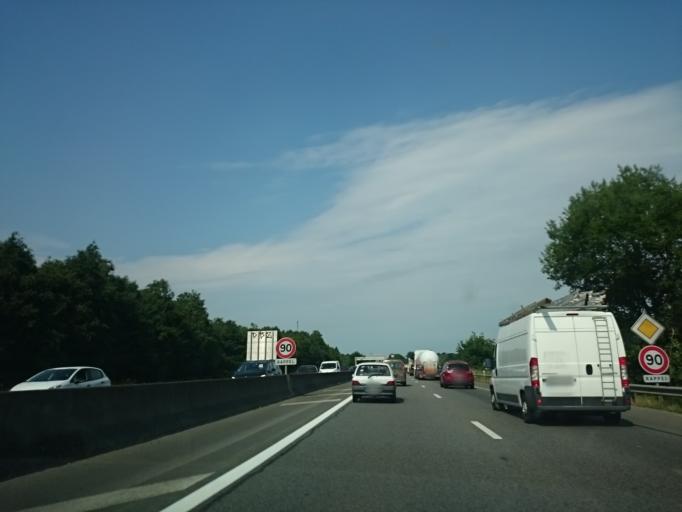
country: FR
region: Brittany
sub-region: Departement d'Ille-et-Vilaine
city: Chantepie
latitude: 48.0861
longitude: -1.6377
